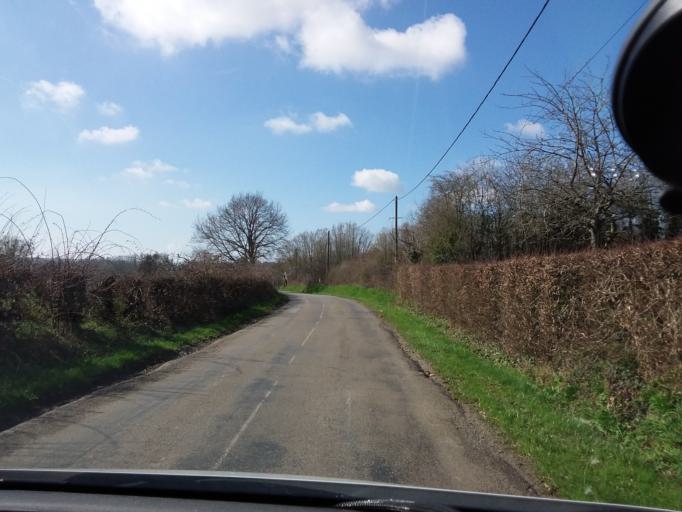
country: FR
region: Picardie
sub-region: Departement de l'Aisne
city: Origny-en-Thierache
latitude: 49.8317
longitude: 4.0527
